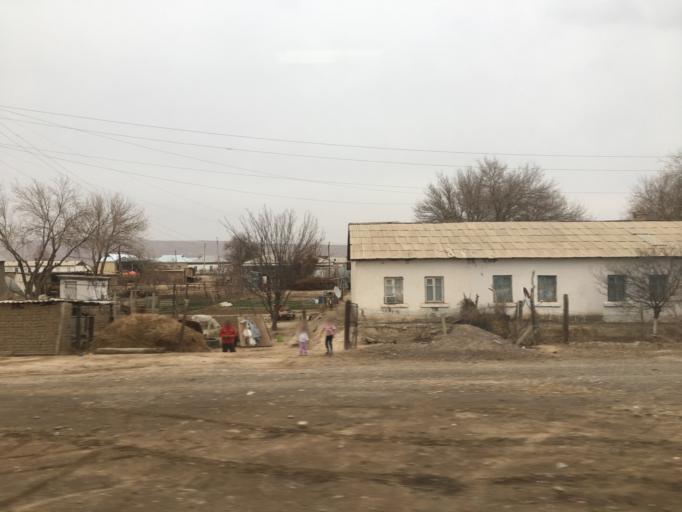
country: TM
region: Mary
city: Yoloeten
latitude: 36.5366
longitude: 62.5540
